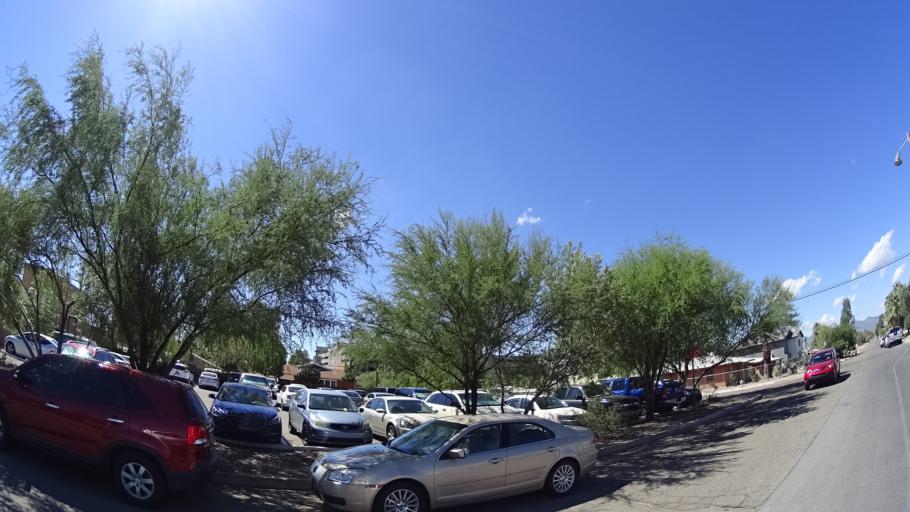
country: US
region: Arizona
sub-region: Pima County
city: Tucson
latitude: 32.2396
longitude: -110.9494
